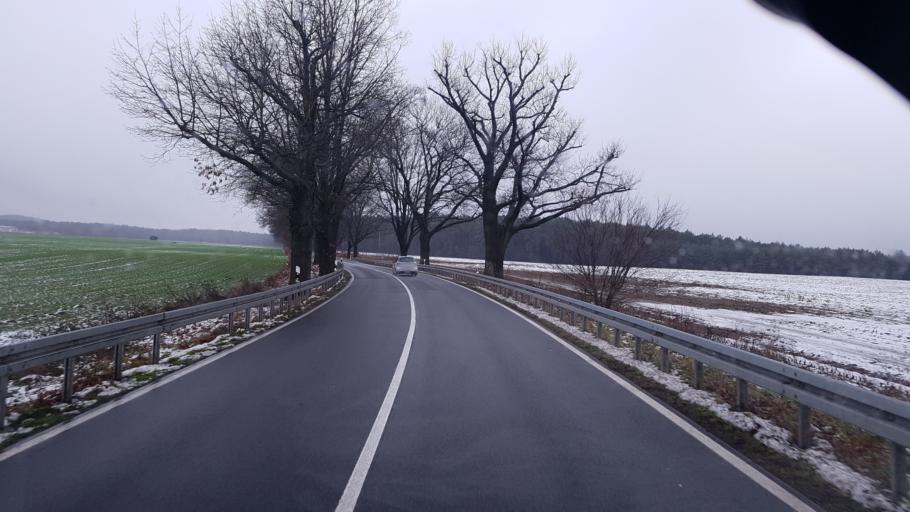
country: DE
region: Brandenburg
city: Schenkendobern
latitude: 51.9597
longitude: 14.5874
